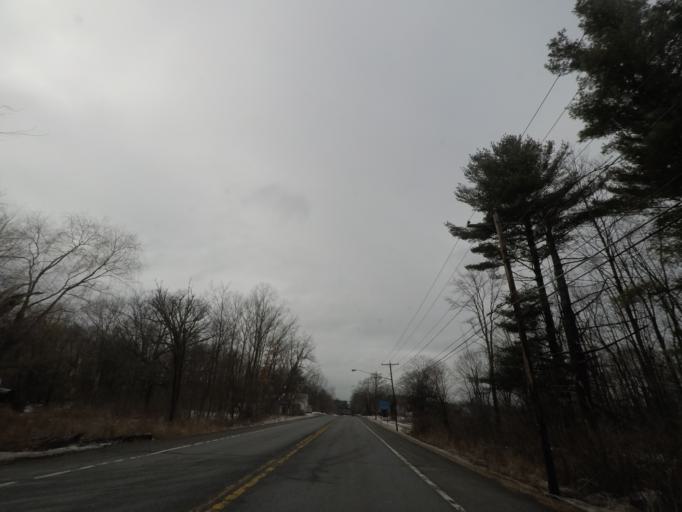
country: US
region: New York
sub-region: Schenectady County
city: Rotterdam
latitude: 42.7236
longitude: -73.9545
